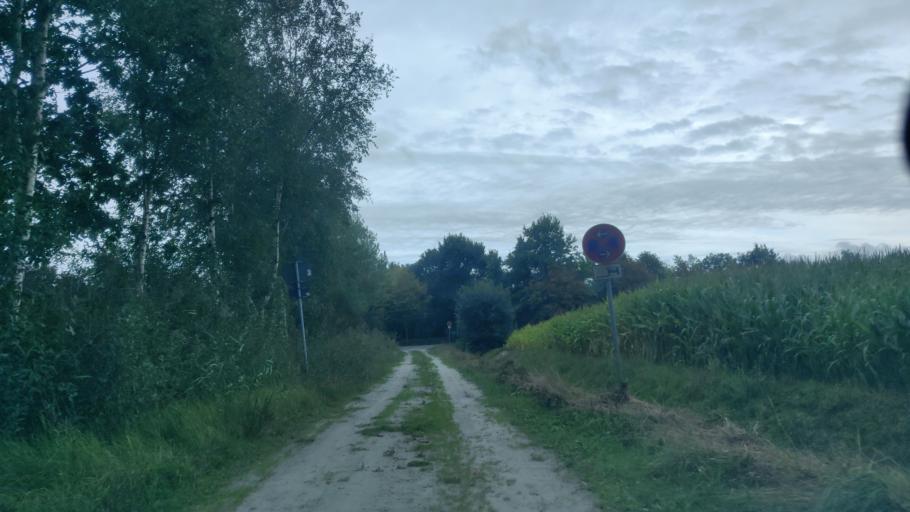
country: DE
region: Lower Saxony
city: Aurich
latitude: 53.5279
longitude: 7.4783
